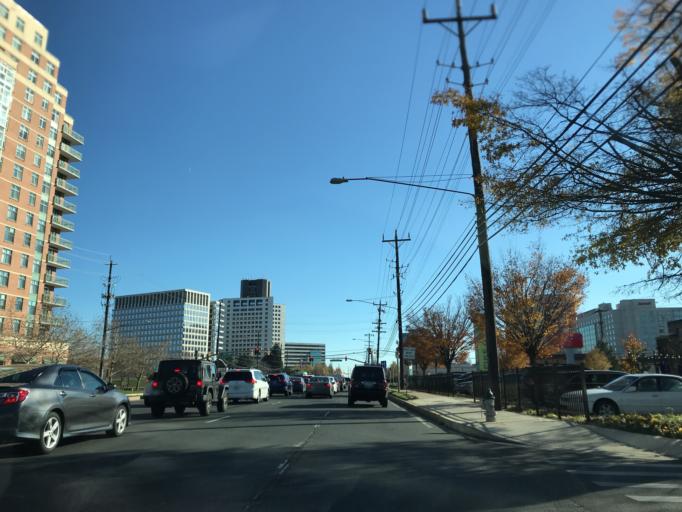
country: US
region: Maryland
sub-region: Montgomery County
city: North Bethesda
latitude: 39.0504
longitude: -77.1151
